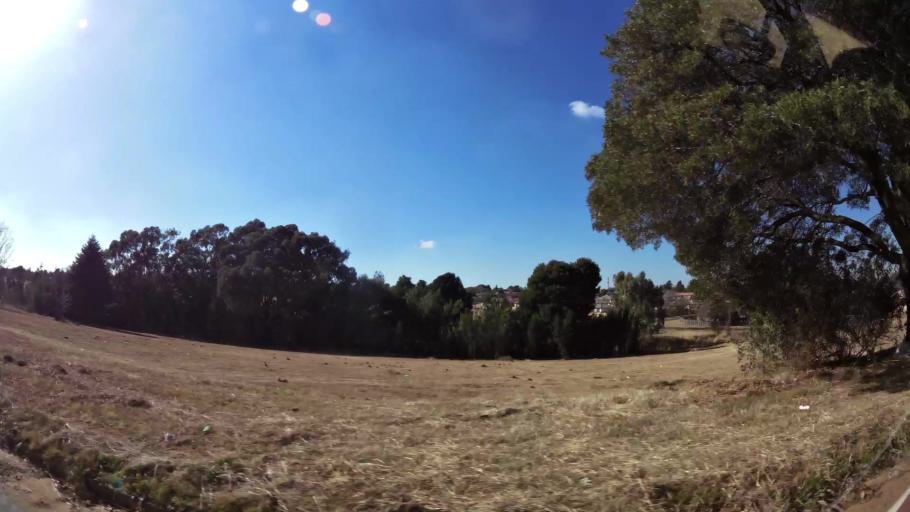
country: ZA
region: Gauteng
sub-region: City of Johannesburg Metropolitan Municipality
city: Roodepoort
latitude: -26.1387
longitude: 27.8211
